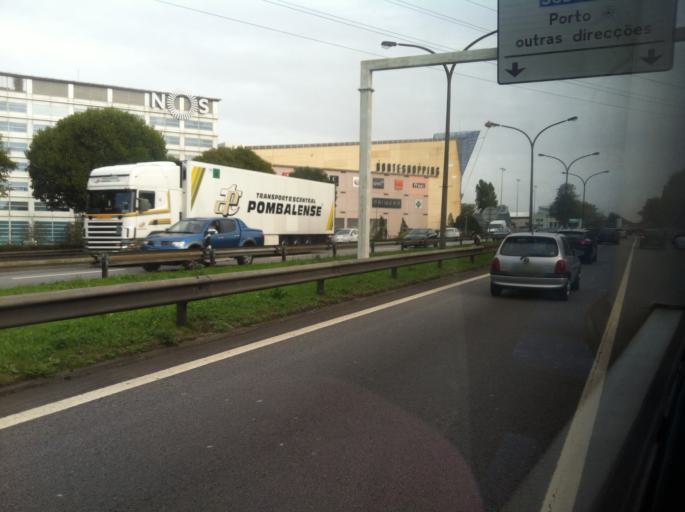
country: PT
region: Porto
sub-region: Matosinhos
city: Senhora da Hora
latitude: 41.1805
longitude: -8.6585
